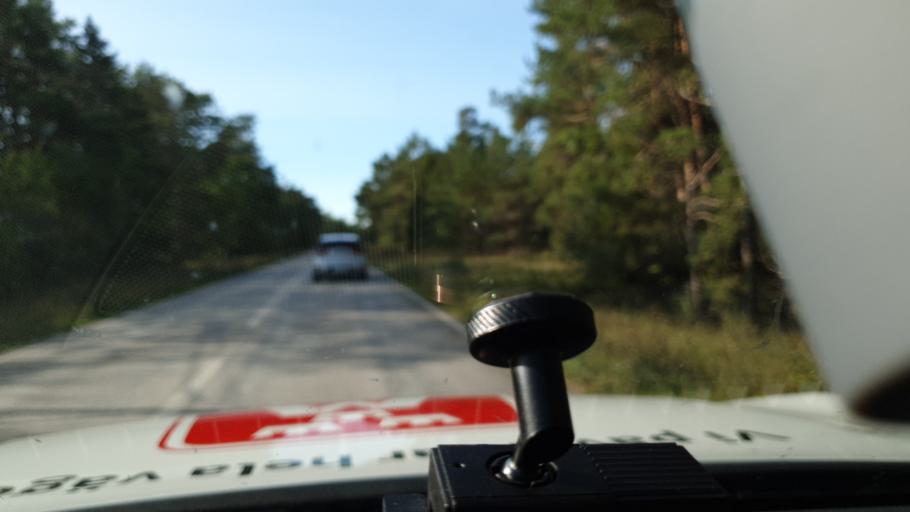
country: SE
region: Gotland
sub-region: Gotland
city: Klintehamn
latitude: 57.3210
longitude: 18.1853
